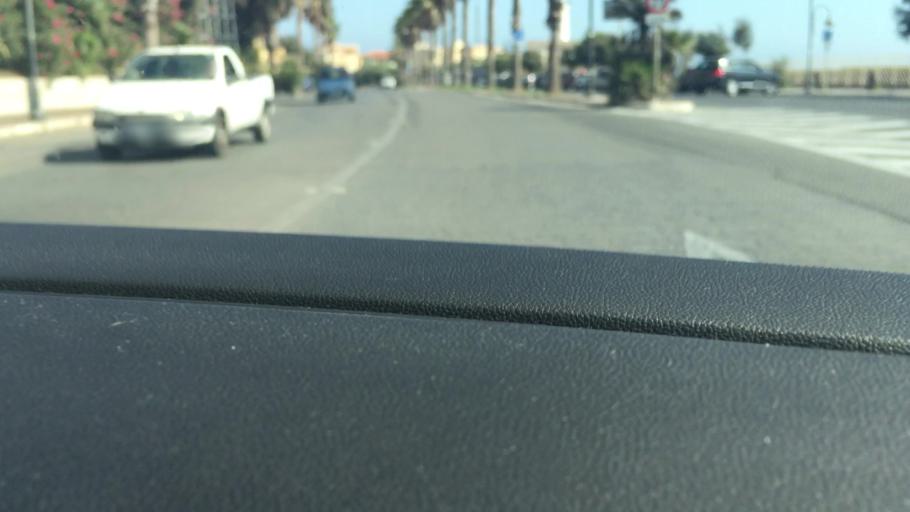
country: IT
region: Latium
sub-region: Citta metropolitana di Roma Capitale
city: Anzio
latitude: 41.4476
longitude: 12.6200
